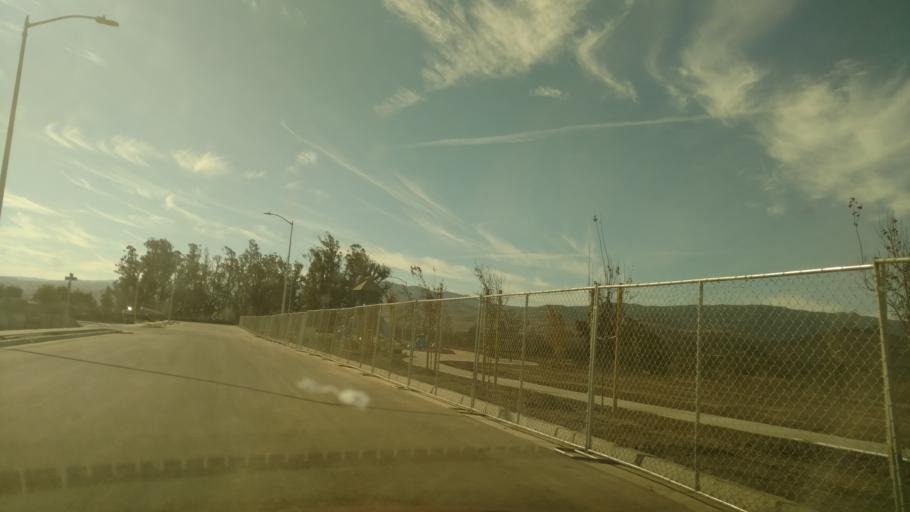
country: US
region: California
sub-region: San Benito County
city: Hollister
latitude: 36.8459
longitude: -121.4195
